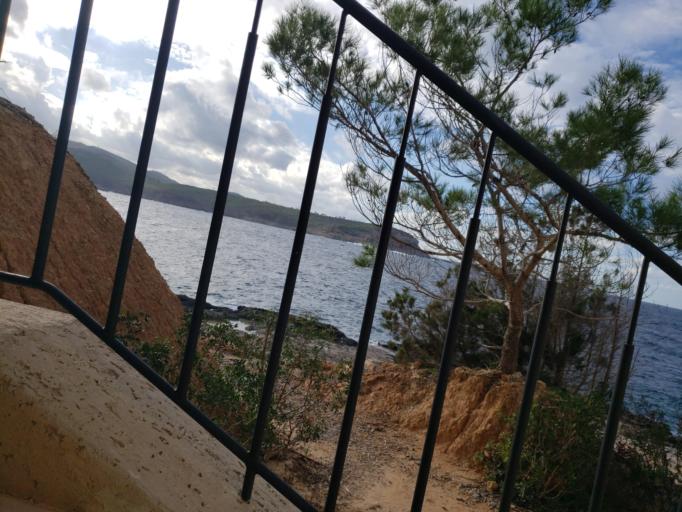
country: ES
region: Balearic Islands
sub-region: Illes Balears
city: Sant Joan de Labritja
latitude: 39.1104
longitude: 1.5071
